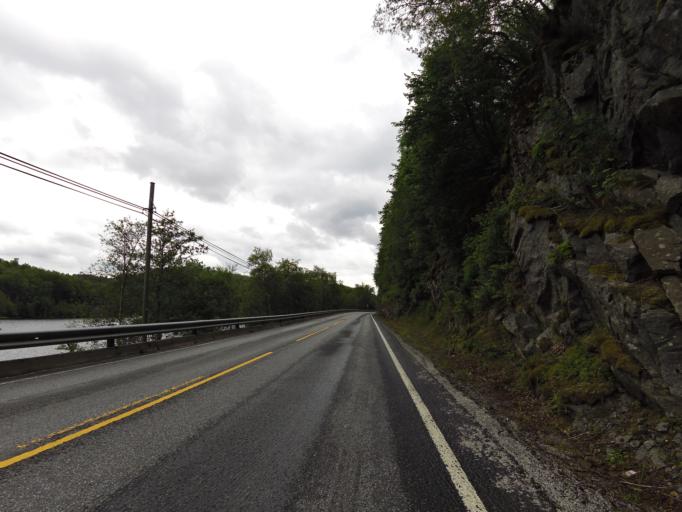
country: NO
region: Vest-Agder
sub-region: Farsund
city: Farsund
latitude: 58.1084
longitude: 6.9236
